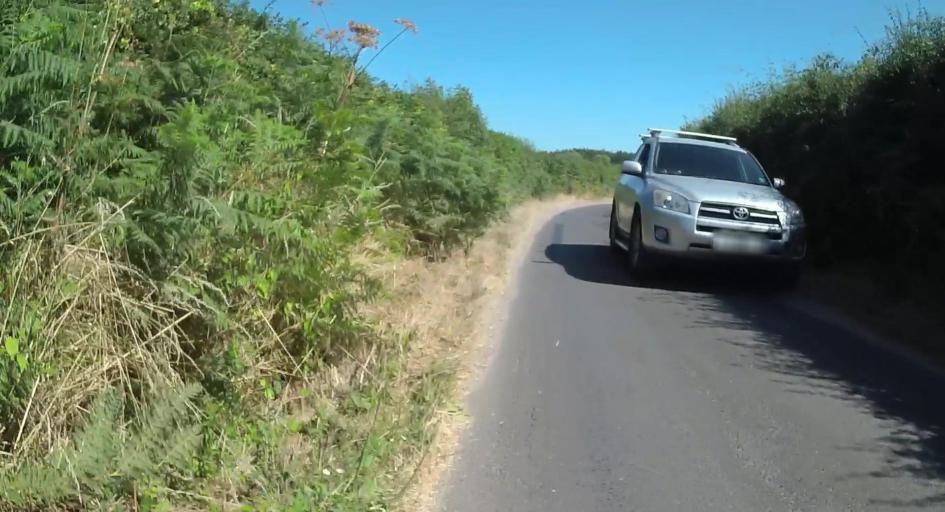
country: GB
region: England
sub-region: Dorset
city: Bovington Camp
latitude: 50.7328
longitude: -2.2057
